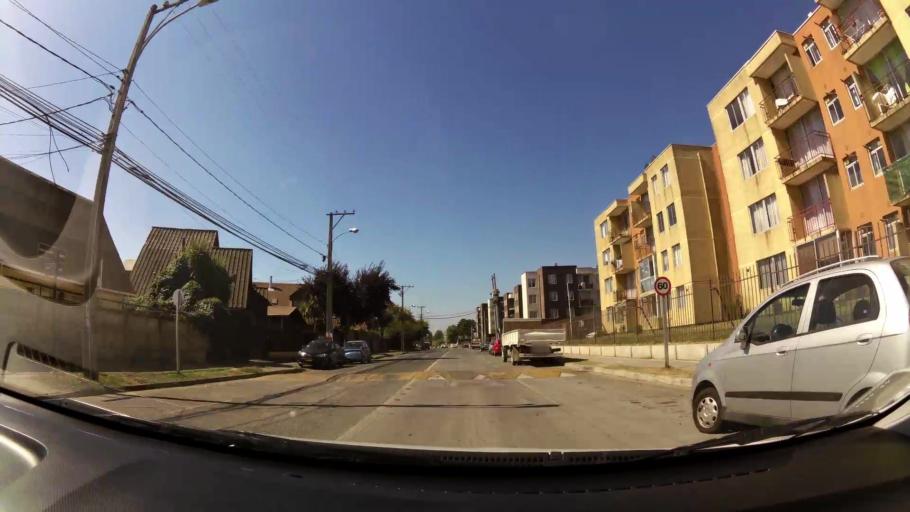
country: CL
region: Biobio
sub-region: Provincia de Concepcion
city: Concepcion
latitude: -36.7913
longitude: -73.0358
